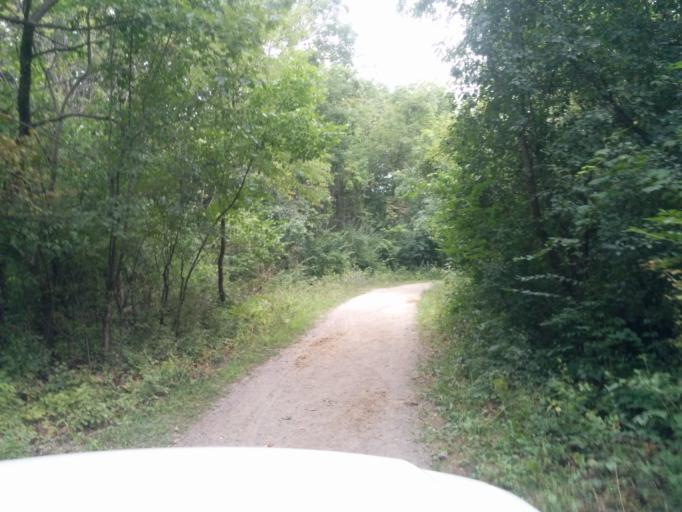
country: US
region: Illinois
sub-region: Cook County
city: Willow Springs
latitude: 41.7408
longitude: -87.8504
